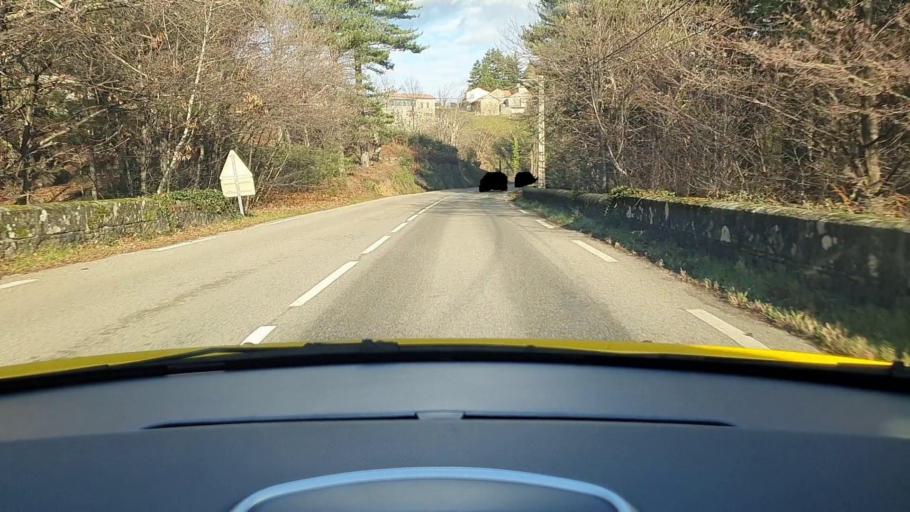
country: FR
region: Languedoc-Roussillon
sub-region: Departement du Gard
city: Branoux-les-Taillades
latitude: 44.3755
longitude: 3.9408
